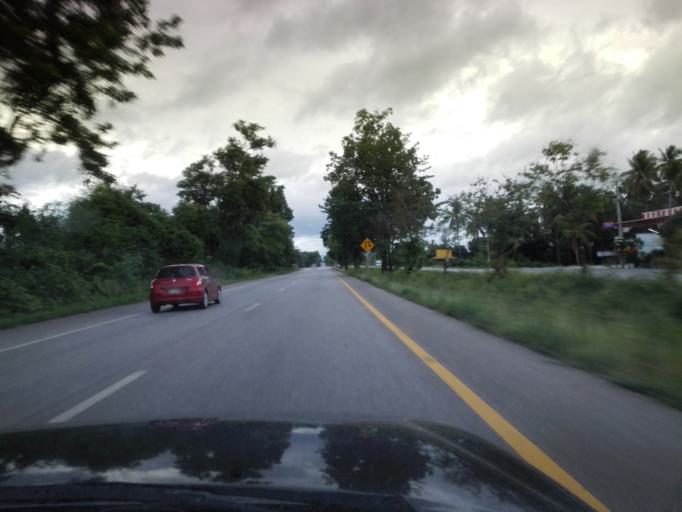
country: TH
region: Tak
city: Tak
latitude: 16.8017
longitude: 99.1480
